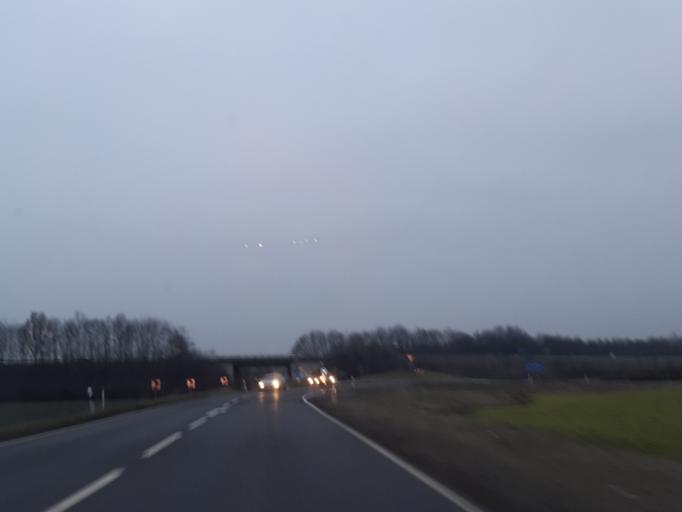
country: DE
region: Bavaria
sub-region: Regierungsbezirk Unterfranken
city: Kleinostheim
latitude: 50.0198
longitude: 9.0492
